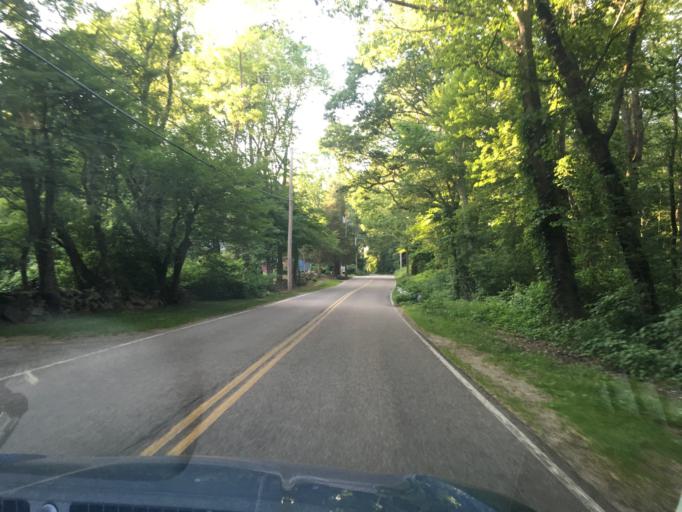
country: US
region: Rhode Island
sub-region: Washington County
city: Exeter
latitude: 41.6138
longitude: -71.5094
